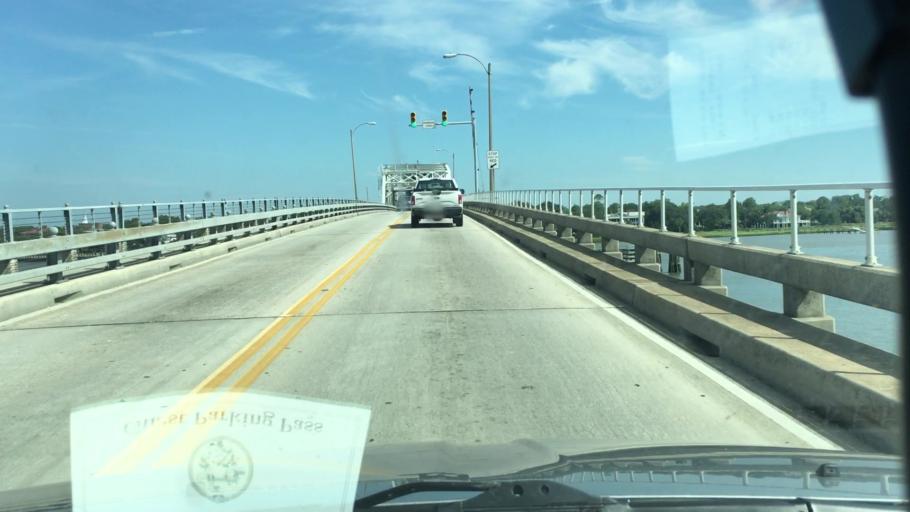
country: US
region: South Carolina
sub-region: Beaufort County
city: Beaufort
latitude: 32.4261
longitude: -80.6688
